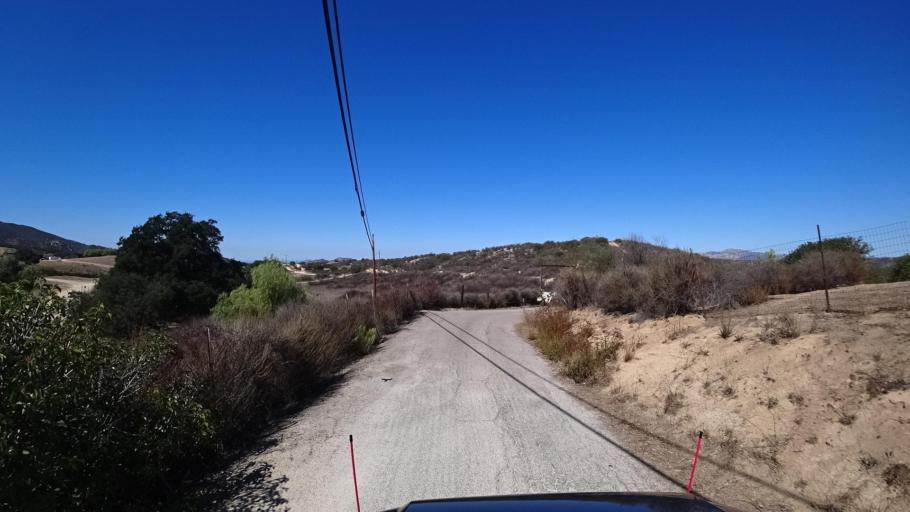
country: US
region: California
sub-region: San Diego County
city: Alpine
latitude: 32.7727
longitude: -116.7714
